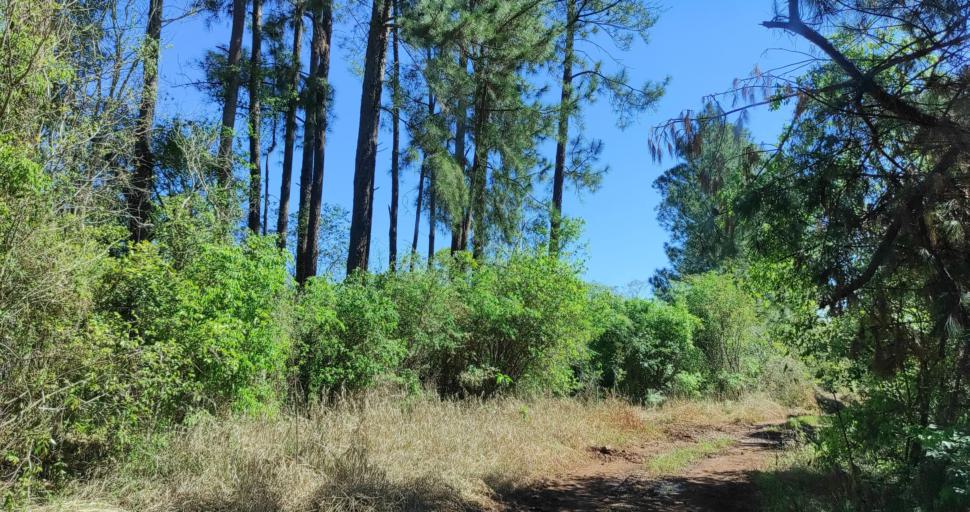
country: AR
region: Misiones
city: Ruiz de Montoya
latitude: -26.9525
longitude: -54.9829
